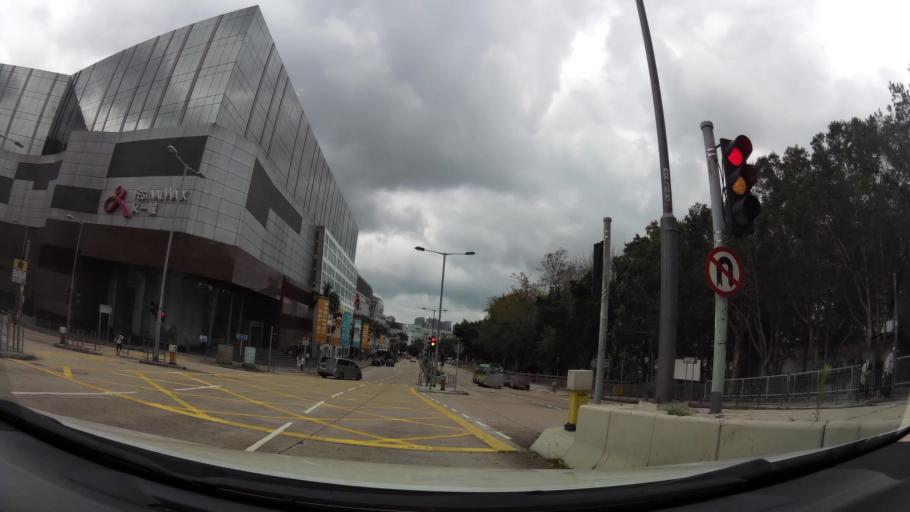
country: HK
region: Sham Shui Po
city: Sham Shui Po
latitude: 22.3377
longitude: 114.1733
